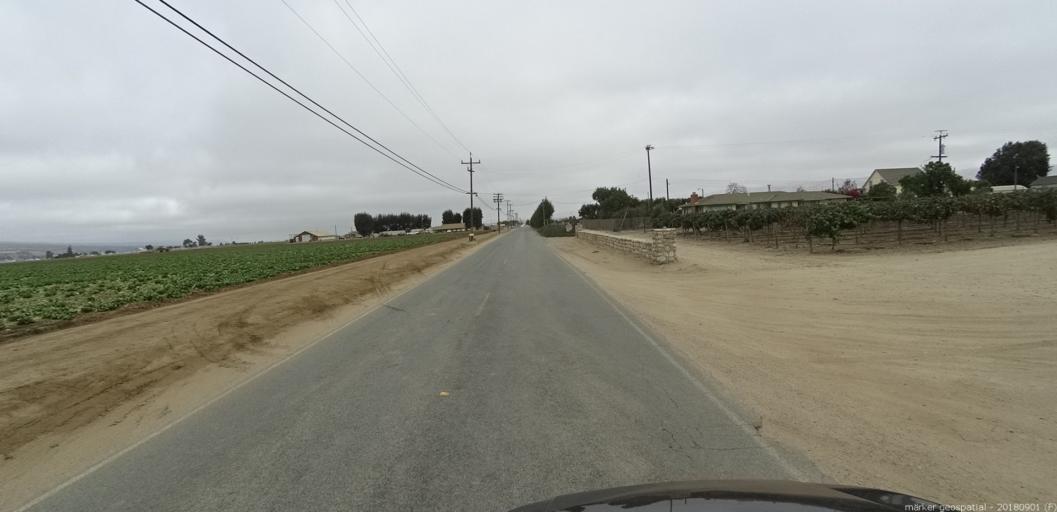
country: US
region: California
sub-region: Monterey County
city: Soledad
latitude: 36.3814
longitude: -121.3291
